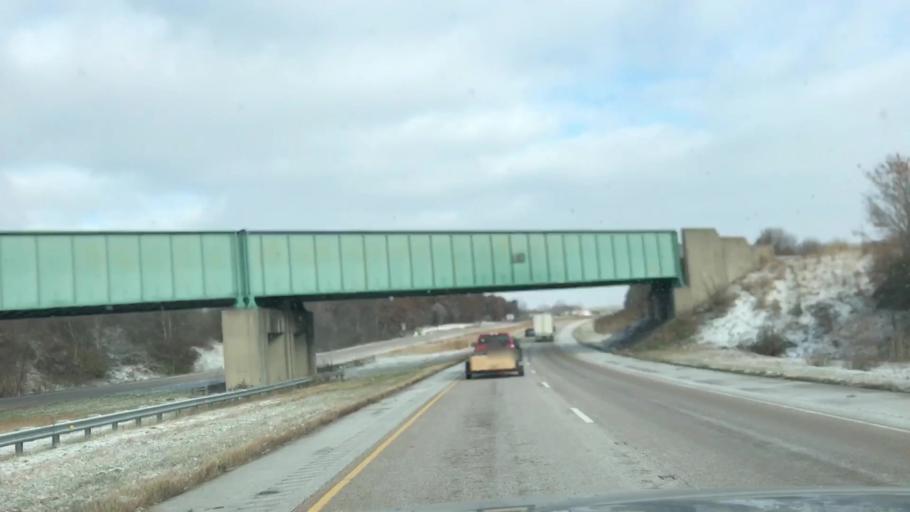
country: US
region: Illinois
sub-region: Macoupin County
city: Staunton
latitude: 39.0357
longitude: -89.7549
